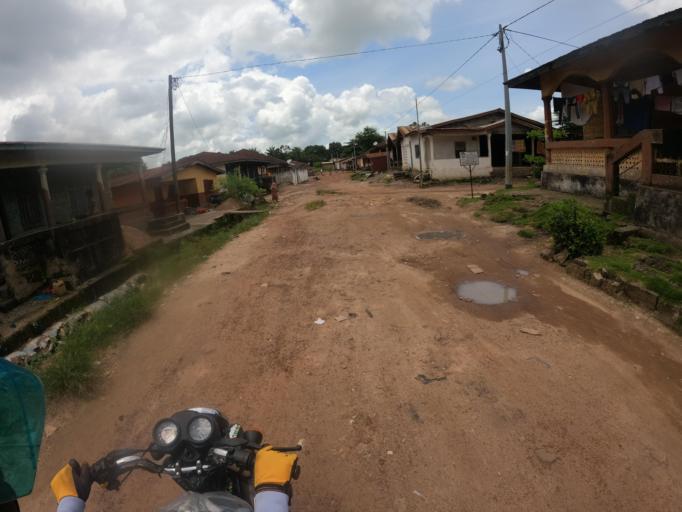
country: SL
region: Northern Province
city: Makeni
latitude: 8.8910
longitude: -12.0529
